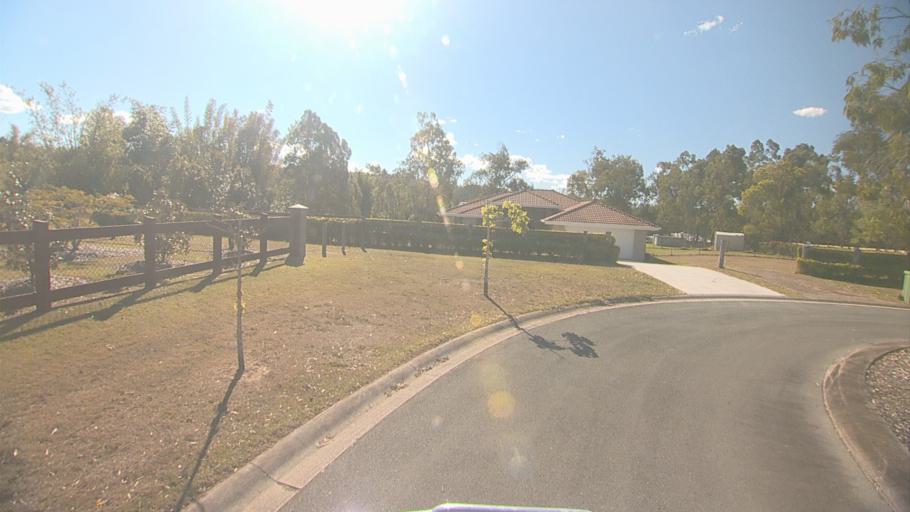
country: AU
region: Queensland
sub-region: Ipswich
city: Springfield Lakes
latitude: -27.7326
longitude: 152.9110
